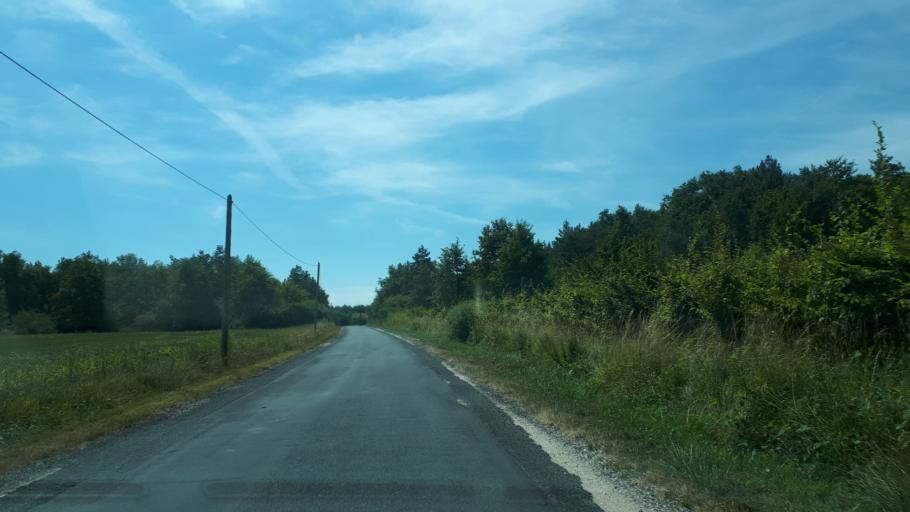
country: FR
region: Centre
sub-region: Departement du Loir-et-Cher
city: Contres
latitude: 47.4213
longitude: 1.3554
